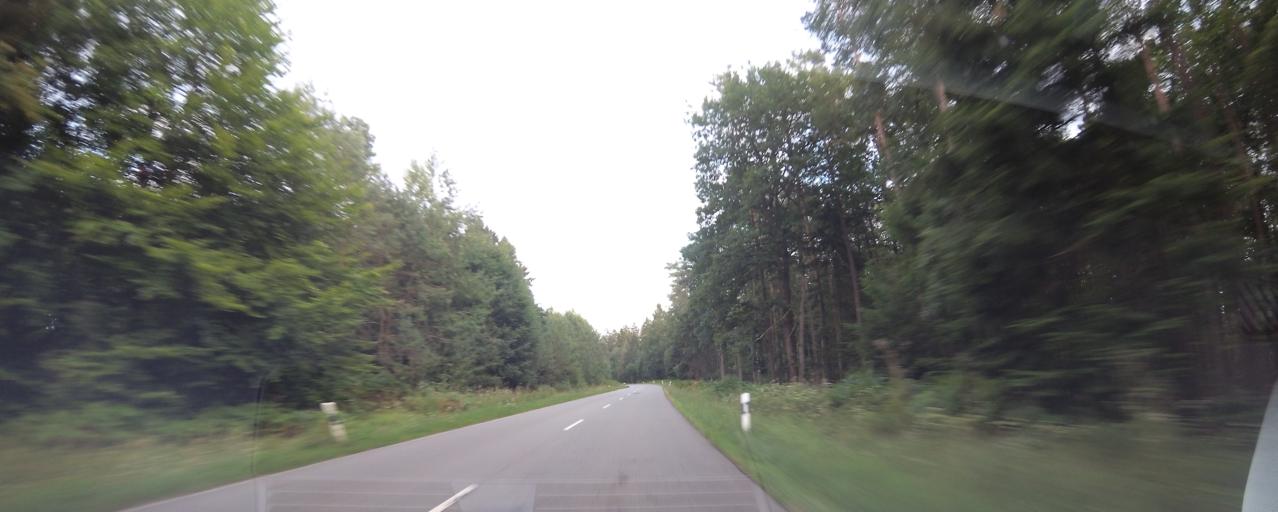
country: DE
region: Rheinland-Pfalz
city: Zemmer
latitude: 49.8828
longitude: 6.7228
